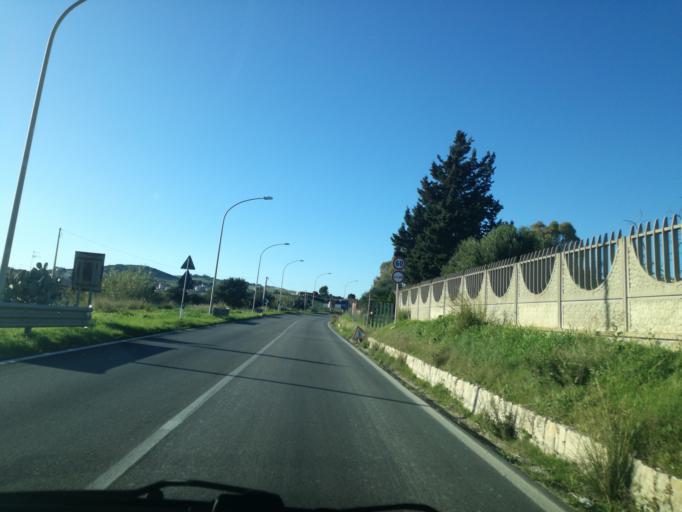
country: IT
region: Sicily
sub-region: Provincia di Caltanissetta
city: Gela
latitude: 37.1003
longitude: 14.1601
